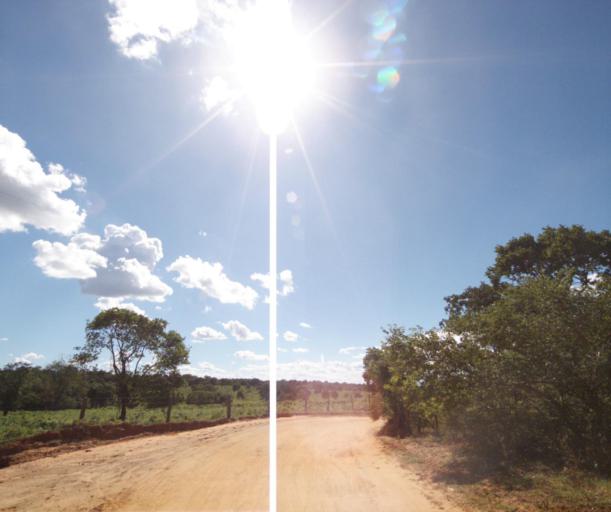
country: BR
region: Bahia
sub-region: Carinhanha
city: Carinhanha
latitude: -14.1874
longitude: -44.4930
